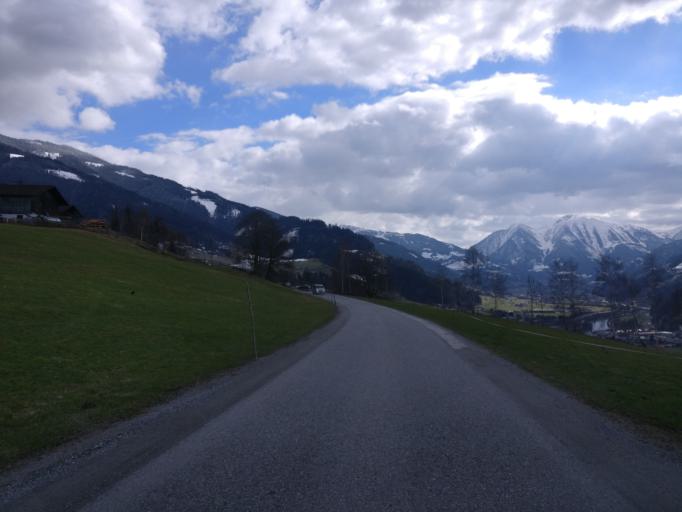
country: AT
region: Salzburg
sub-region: Politischer Bezirk Sankt Johann im Pongau
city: Bischofshofen
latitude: 47.4098
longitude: 13.2283
